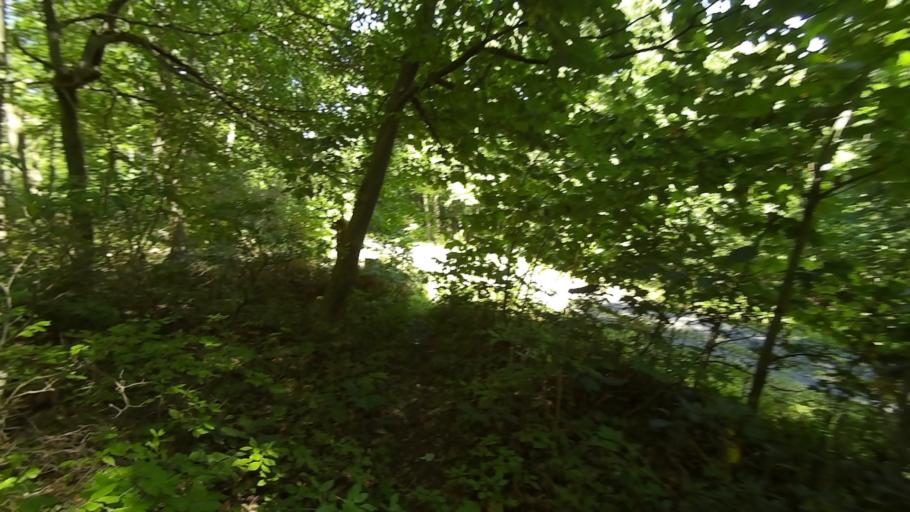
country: US
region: Pennsylvania
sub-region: Centre County
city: Boalsburg
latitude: 40.7344
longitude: -77.7727
